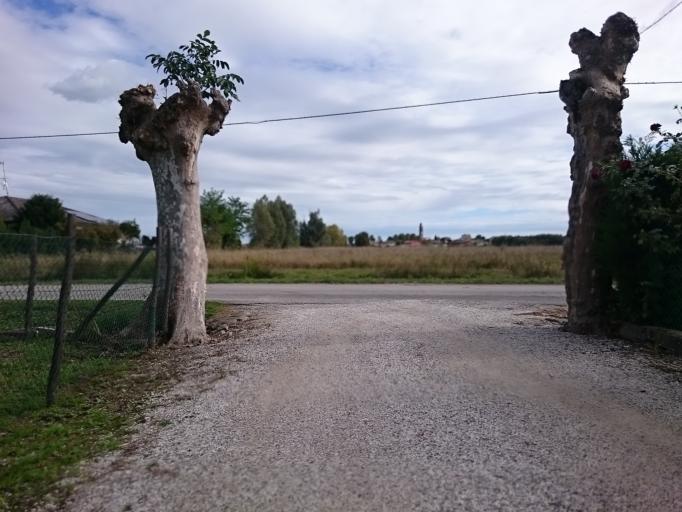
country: IT
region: Veneto
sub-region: Provincia di Padova
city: Bovolenta
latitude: 45.2486
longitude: 11.9356
